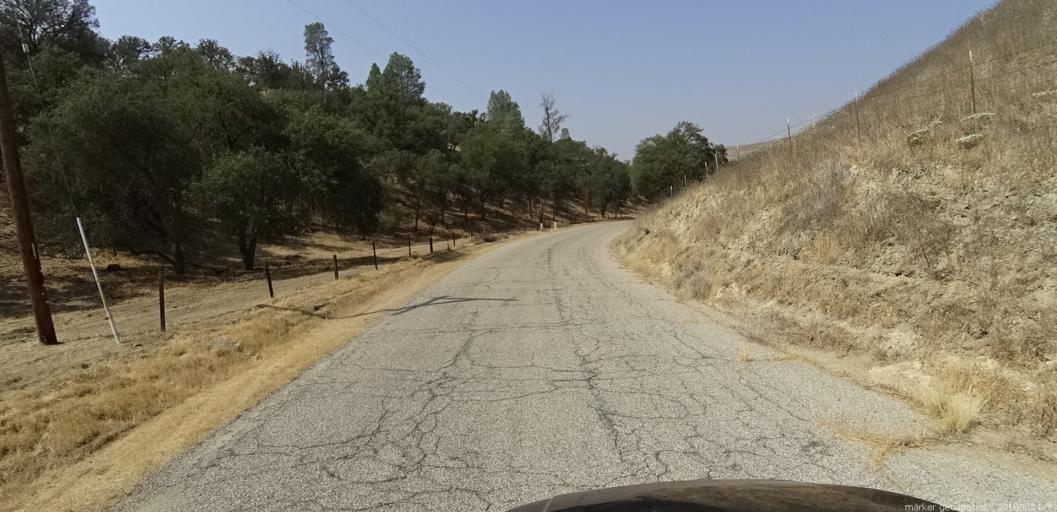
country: US
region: California
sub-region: San Luis Obispo County
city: San Miguel
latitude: 35.8737
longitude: -120.6944
